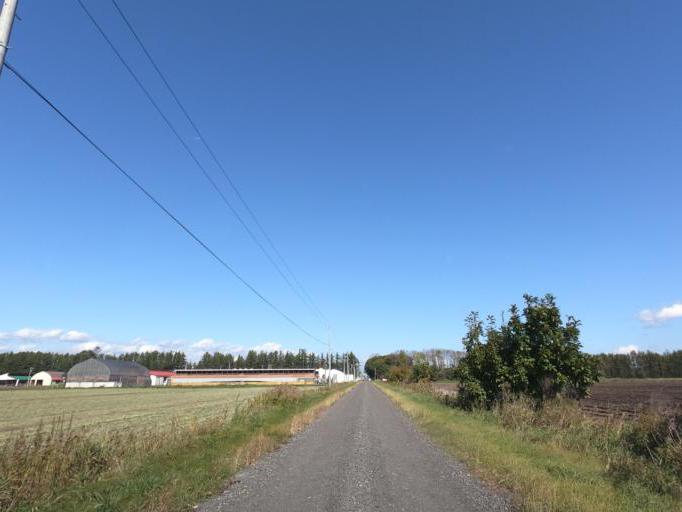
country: JP
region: Hokkaido
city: Otofuke
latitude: 43.0728
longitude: 143.2591
